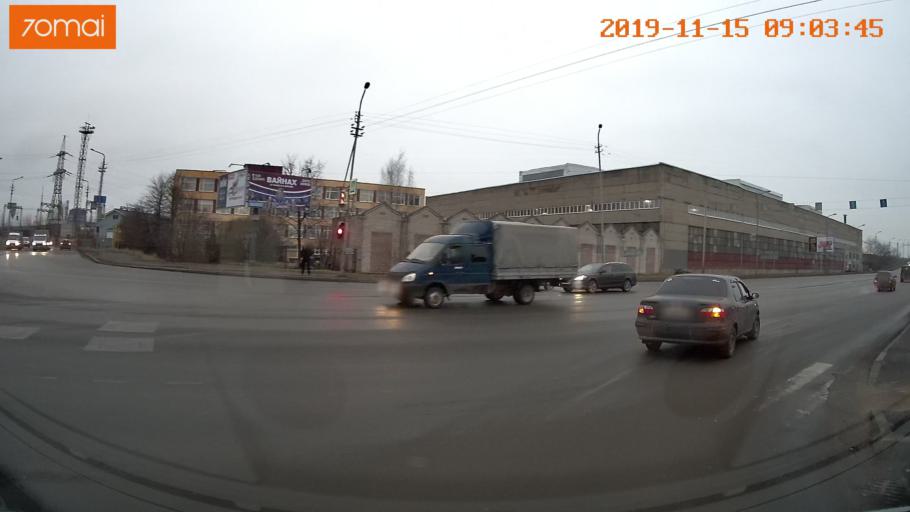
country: RU
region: Vologda
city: Cherepovets
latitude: 59.1396
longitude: 37.9191
